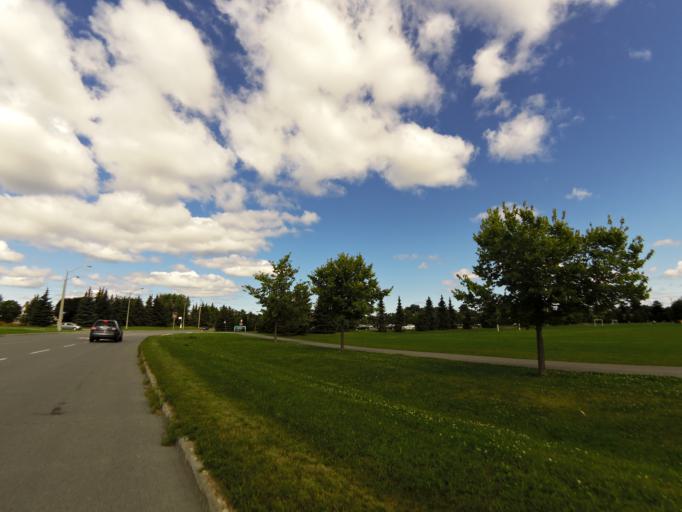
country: CA
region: Ontario
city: Bells Corners
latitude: 45.3248
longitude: -75.7720
